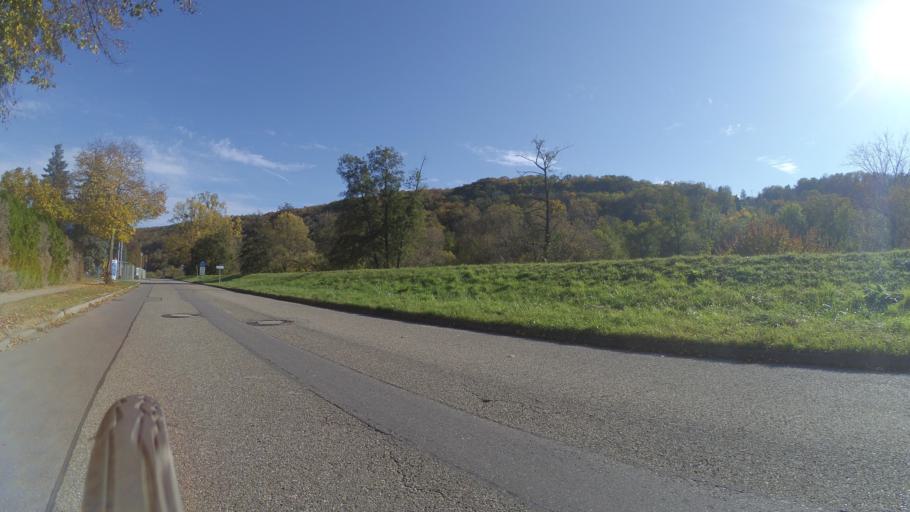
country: DE
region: Baden-Wuerttemberg
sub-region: Regierungsbezirk Stuttgart
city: Forchtenberg
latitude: 49.2912
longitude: 9.5711
